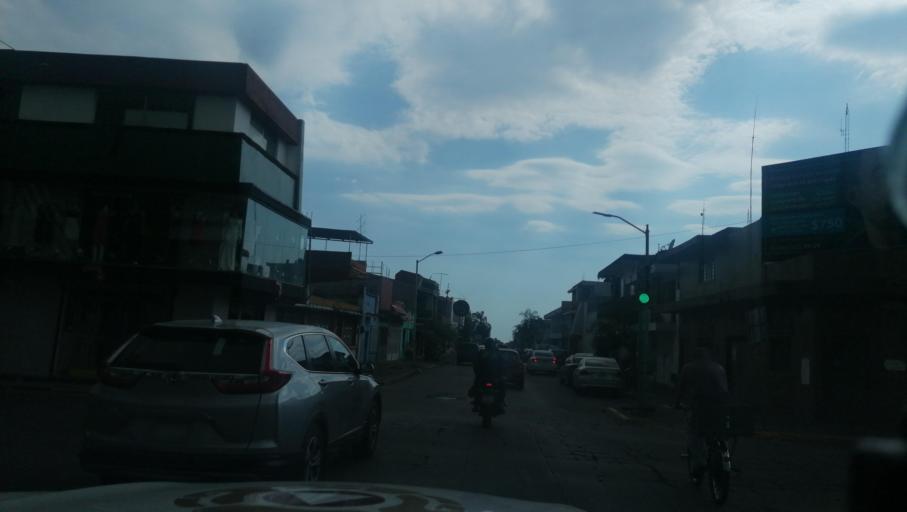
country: MX
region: Chiapas
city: Tapachula
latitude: 14.9126
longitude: -92.2552
